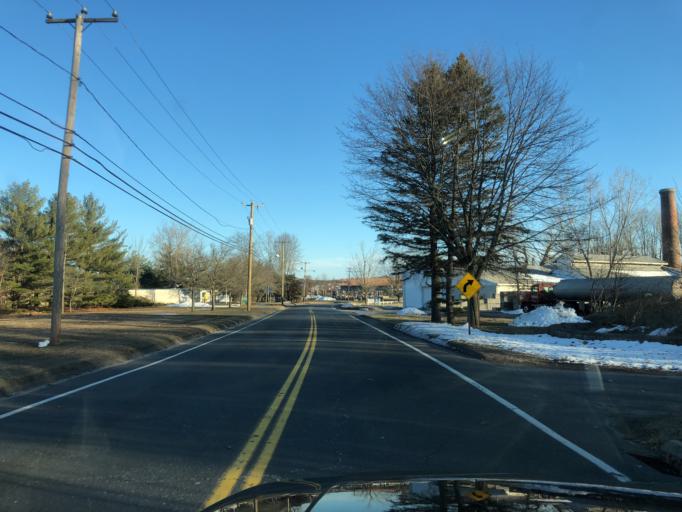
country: US
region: Connecticut
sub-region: Hartford County
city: Farmington
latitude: 41.7533
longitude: -72.8566
